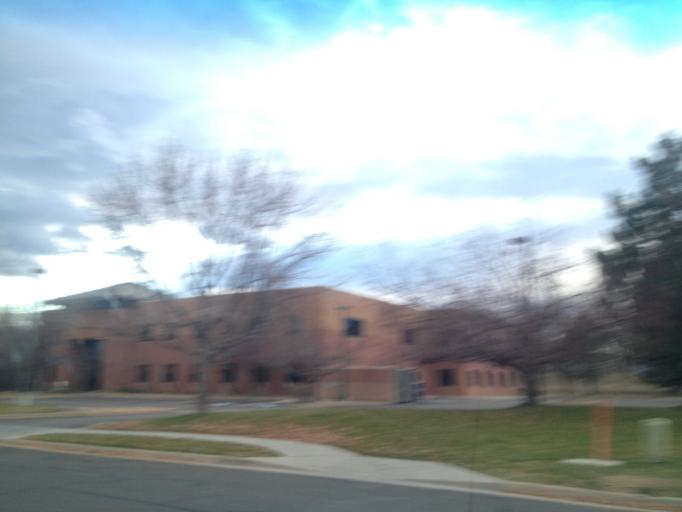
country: US
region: Colorado
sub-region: Boulder County
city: Louisville
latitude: 39.9650
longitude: -105.1246
